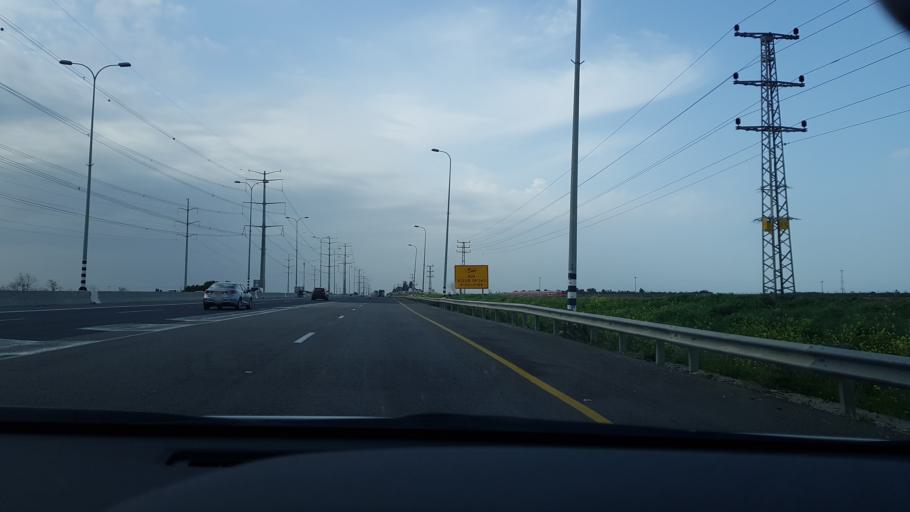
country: IL
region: Central District
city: Gan Yavne
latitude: 31.8074
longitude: 34.6944
